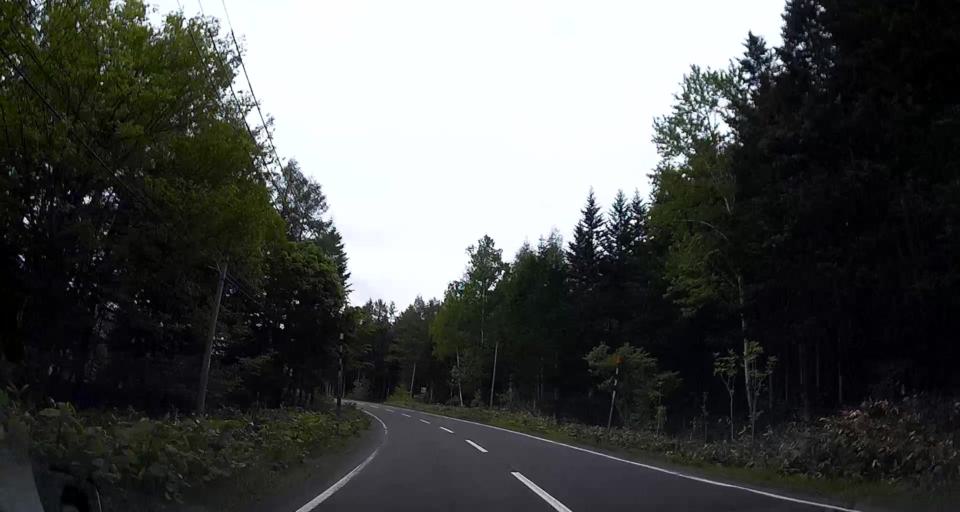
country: JP
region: Hokkaido
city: Shiraoi
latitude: 42.6825
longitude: 141.1008
